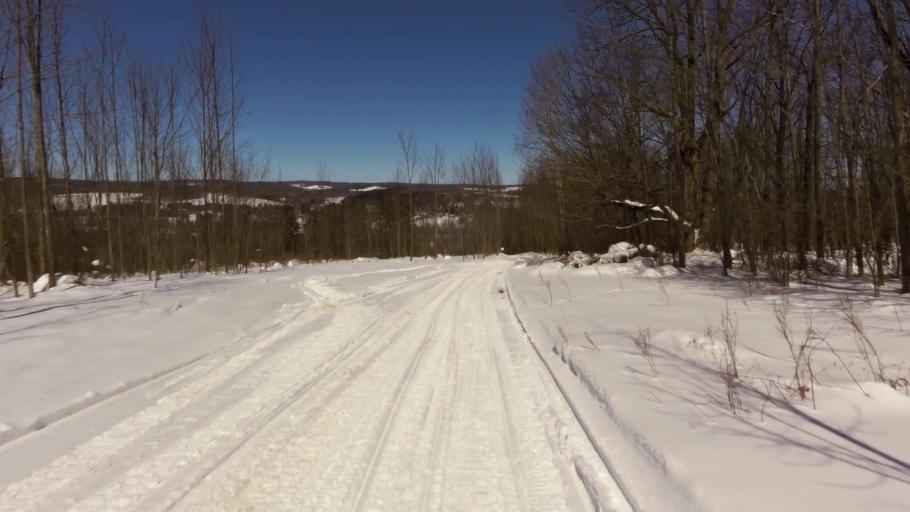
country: US
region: New York
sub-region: Allegany County
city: Houghton
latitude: 42.3773
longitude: -78.2471
